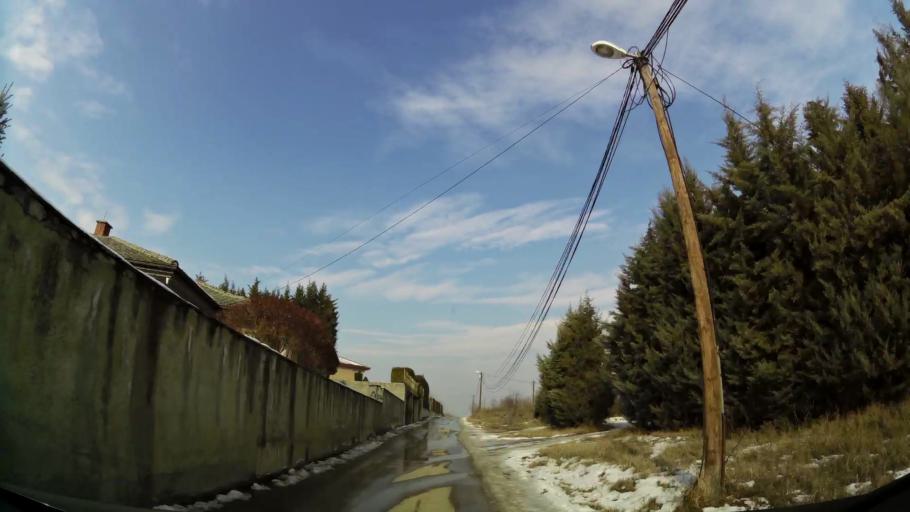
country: MK
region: Suto Orizari
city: Suto Orizare
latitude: 42.0310
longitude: 21.3773
